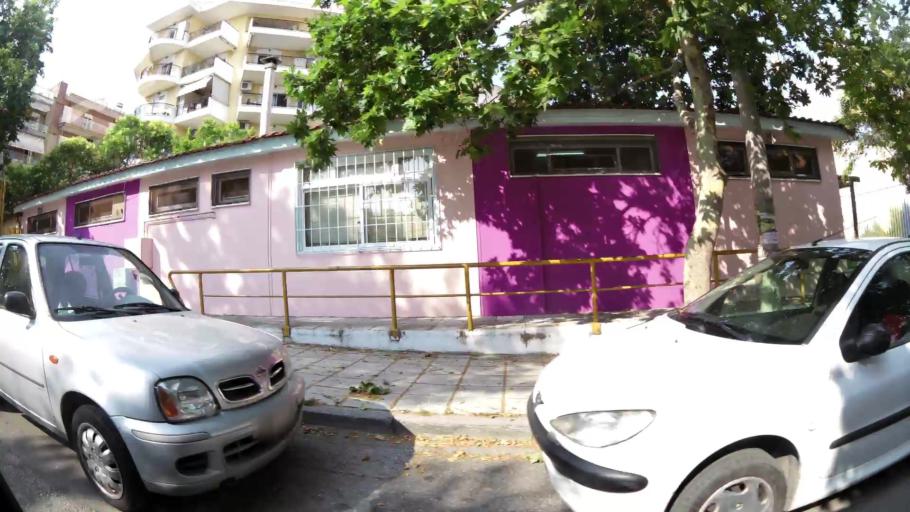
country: GR
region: Central Macedonia
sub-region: Nomos Thessalonikis
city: Sykies
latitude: 40.6533
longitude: 22.9460
